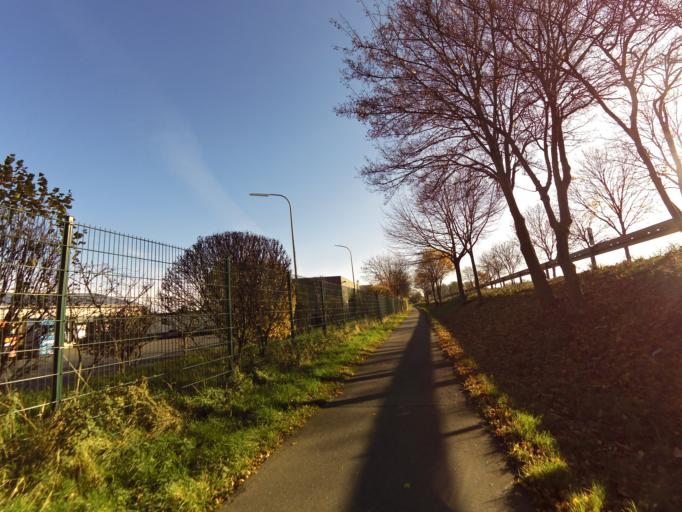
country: DE
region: North Rhine-Westphalia
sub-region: Regierungsbezirk Koln
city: Euskirchen
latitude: 50.6471
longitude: 6.8193
